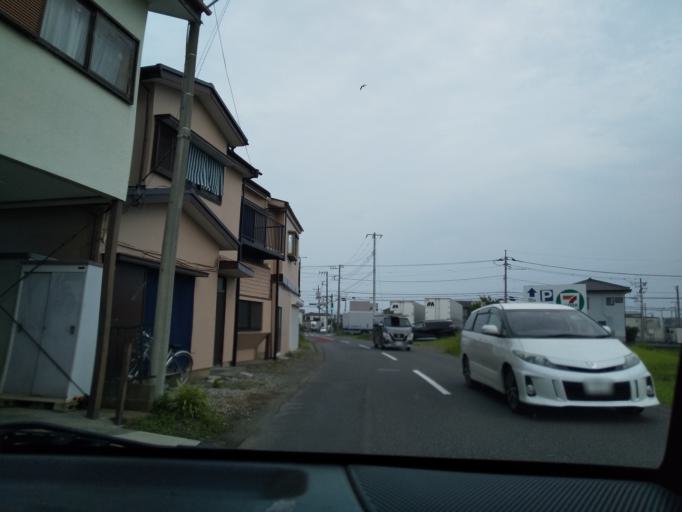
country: JP
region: Kanagawa
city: Atsugi
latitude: 35.3933
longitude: 139.3853
